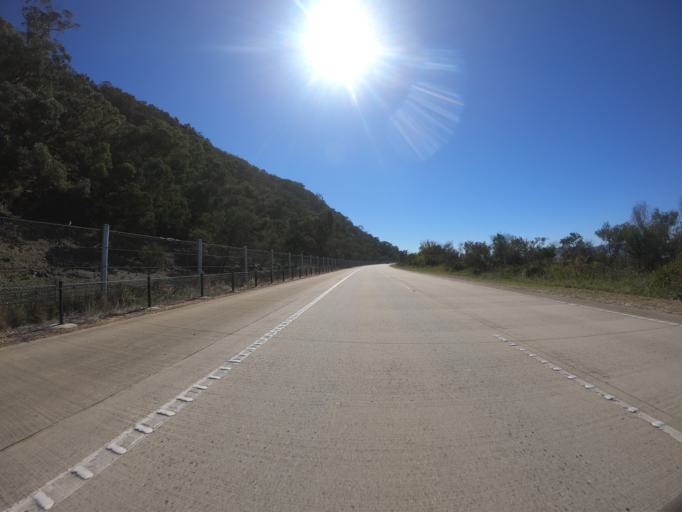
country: AU
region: New South Wales
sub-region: Yass Valley
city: Gundaroo
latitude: -35.0642
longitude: 149.3733
